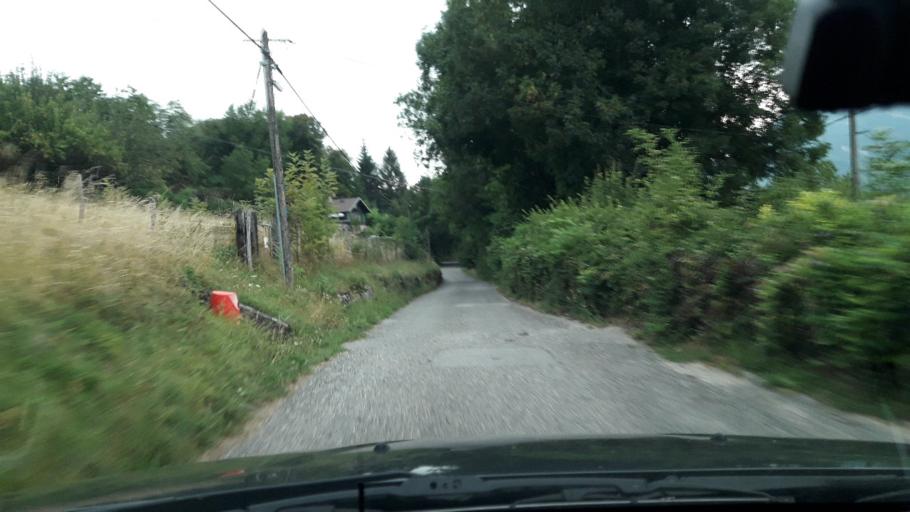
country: FR
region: Rhone-Alpes
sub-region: Departement de la Savoie
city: Barberaz
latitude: 45.5498
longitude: 5.9363
